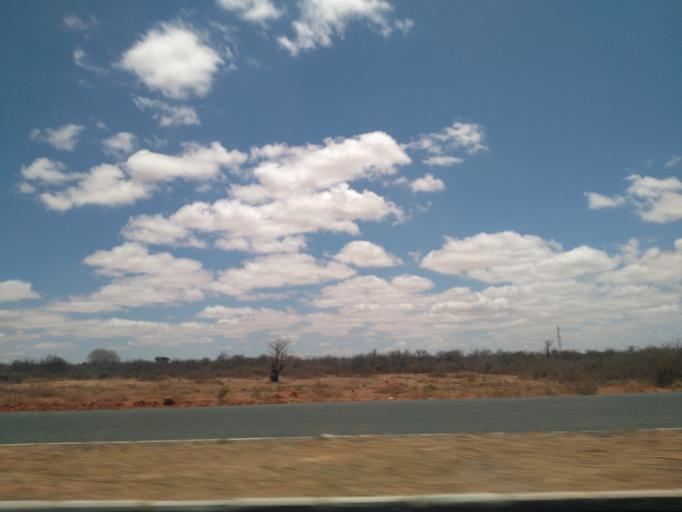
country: TZ
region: Dodoma
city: Kisasa
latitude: -6.1693
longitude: 35.8423
